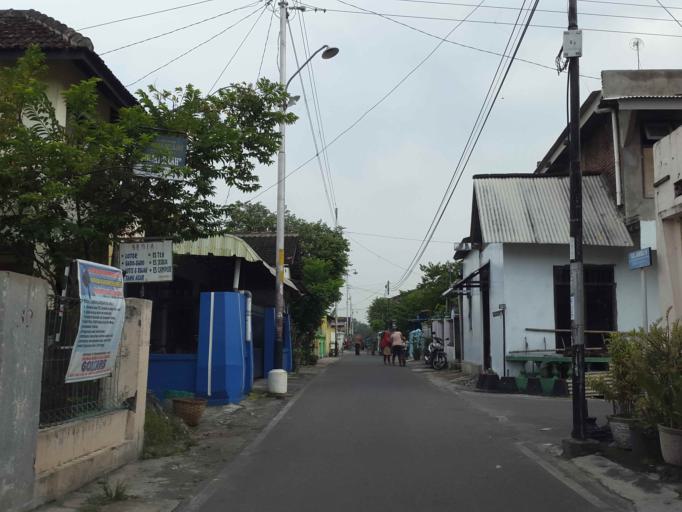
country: ID
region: Central Java
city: Colomadu
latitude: -7.5547
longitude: 110.7836
